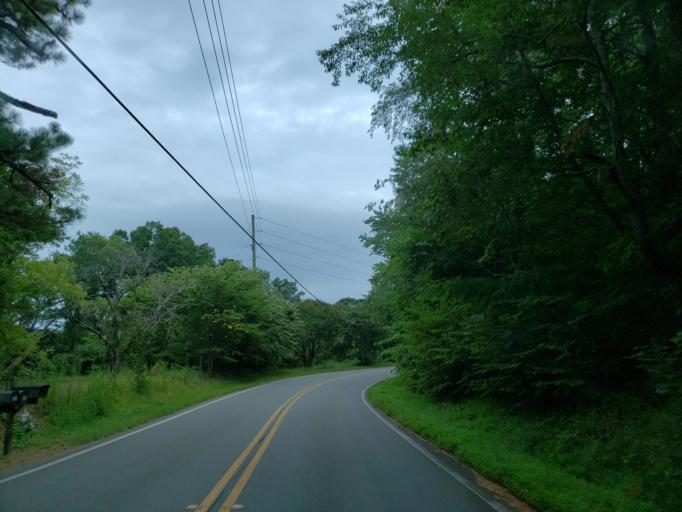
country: US
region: Georgia
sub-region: Pickens County
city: Jasper
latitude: 34.4192
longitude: -84.5755
